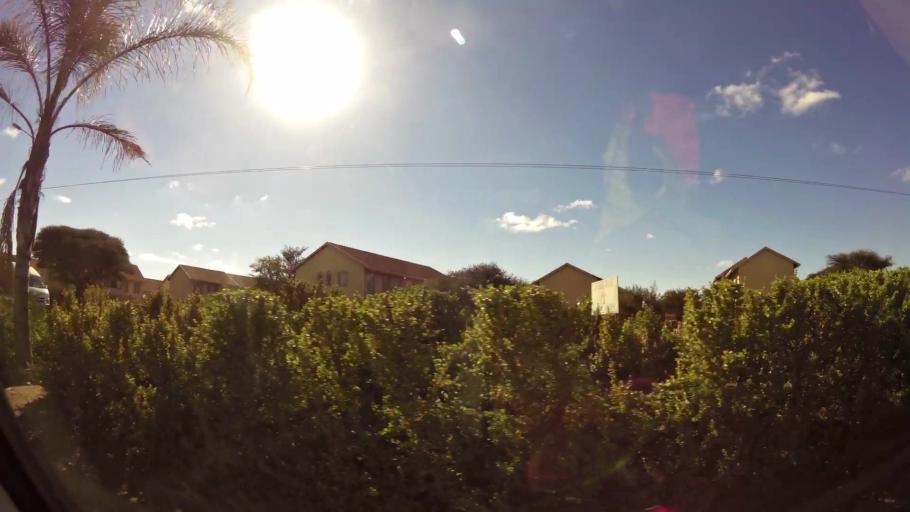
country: ZA
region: Limpopo
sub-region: Capricorn District Municipality
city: Polokwane
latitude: -23.8839
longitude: 29.4435
